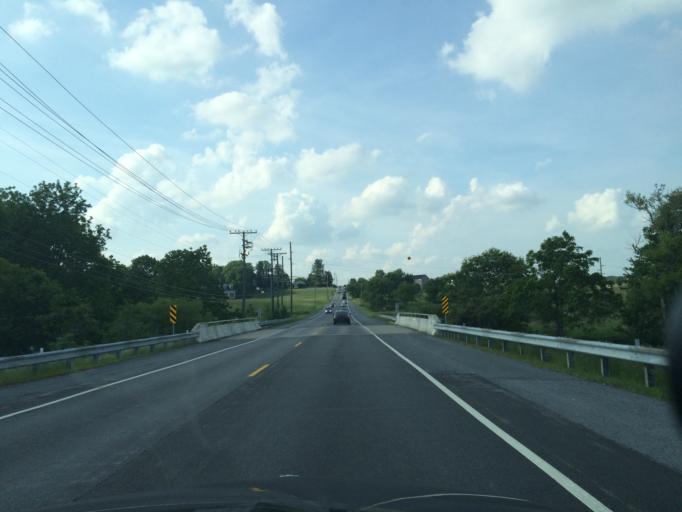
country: US
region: Maryland
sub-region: Carroll County
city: Sykesville
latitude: 39.3804
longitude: -77.0187
